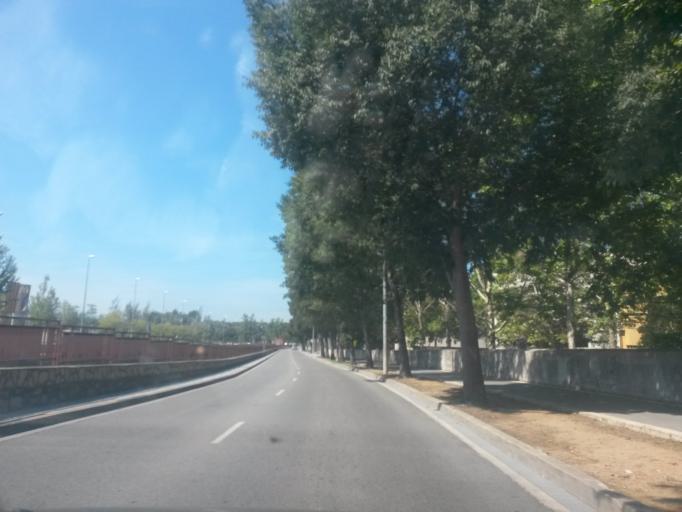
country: ES
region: Catalonia
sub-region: Provincia de Girona
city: Girona
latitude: 41.9813
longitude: 2.8111
